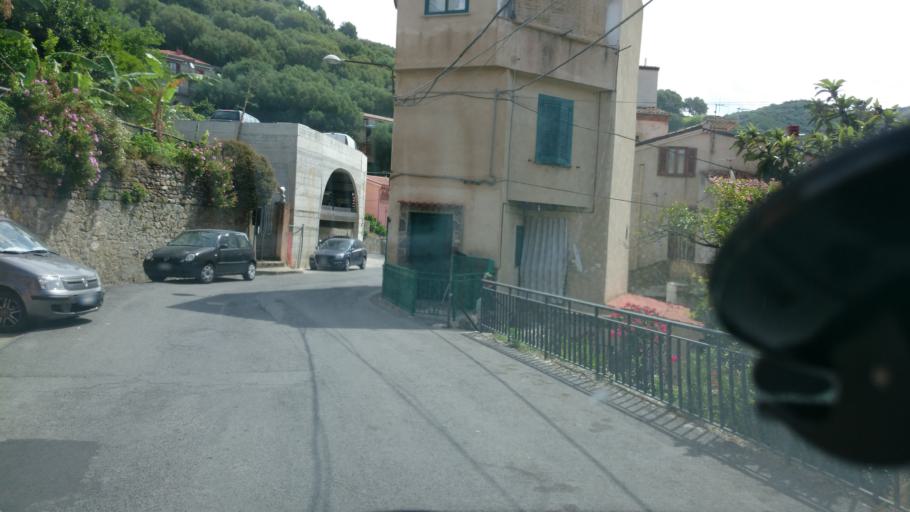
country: IT
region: Campania
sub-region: Provincia di Salerno
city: Pisciotta
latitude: 40.1090
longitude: 15.2338
